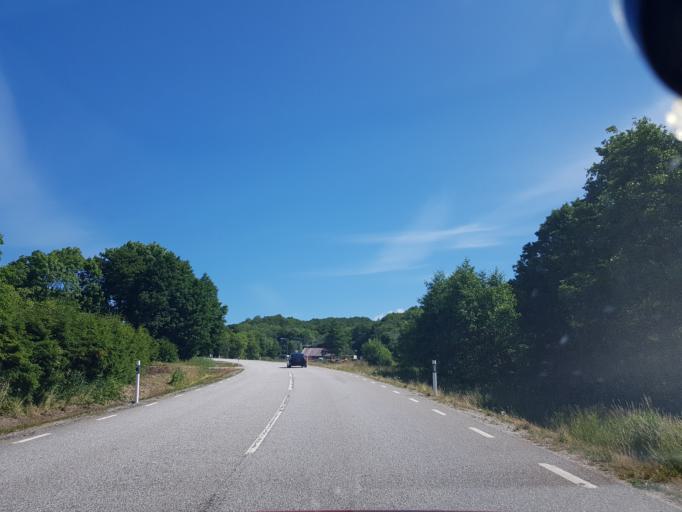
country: SE
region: Vaestra Goetaland
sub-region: Lysekils Kommun
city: Lysekil
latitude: 58.1549
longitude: 11.4683
